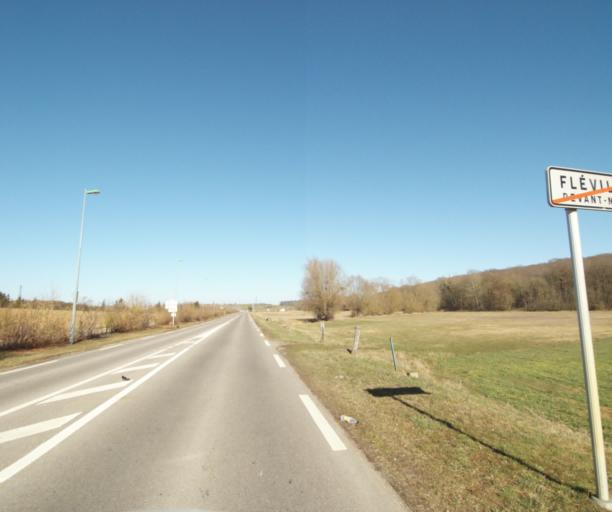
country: FR
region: Lorraine
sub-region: Departement de Meurthe-et-Moselle
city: Fleville-devant-Nancy
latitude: 48.6322
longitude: 6.2103
